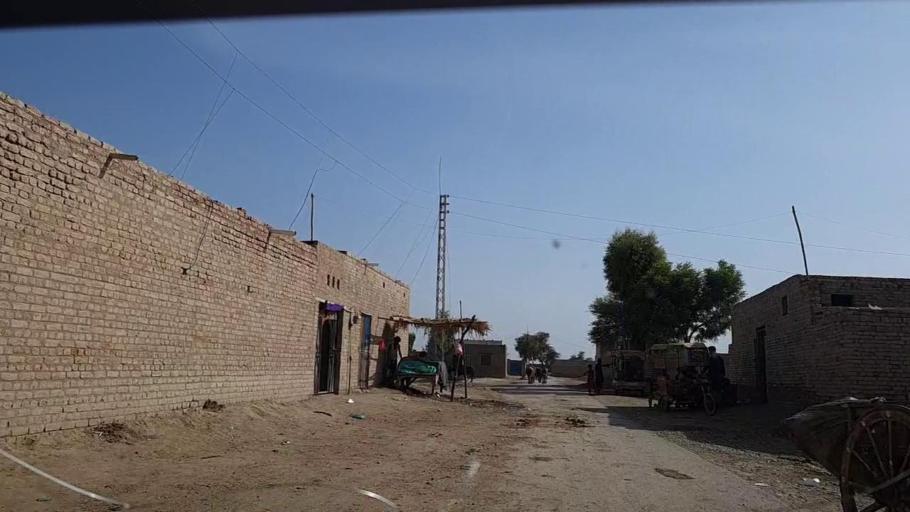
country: PK
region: Sindh
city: Phulji
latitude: 26.9917
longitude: 67.6640
